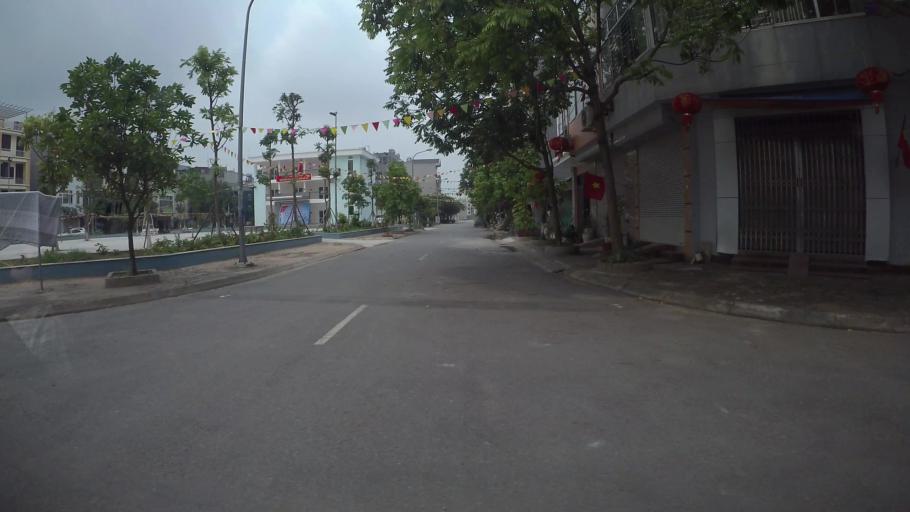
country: VN
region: Ha Noi
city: Trau Quy
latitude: 21.0646
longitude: 105.9167
